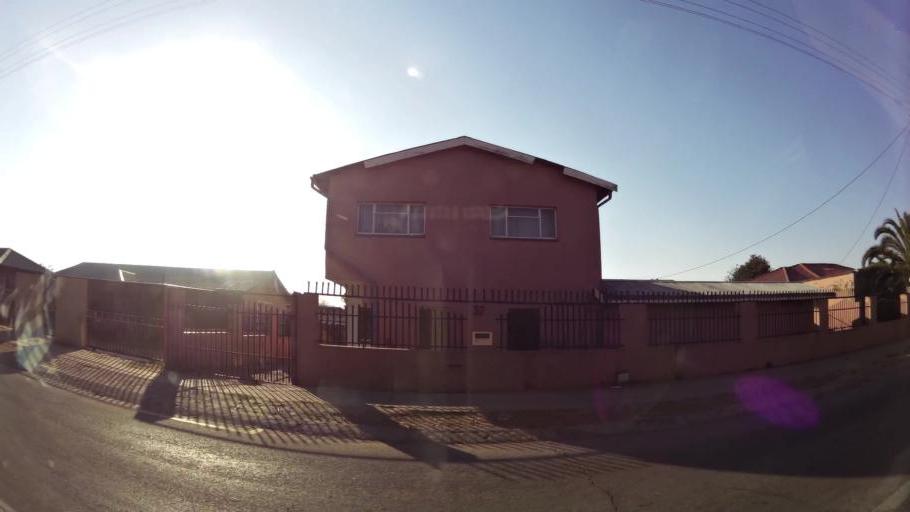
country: ZA
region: Gauteng
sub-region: City of Tshwane Metropolitan Municipality
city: Pretoria
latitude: -25.7575
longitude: 28.1227
